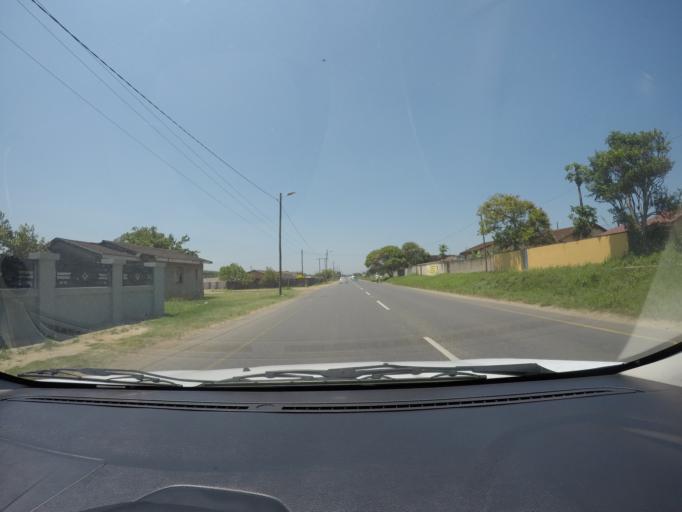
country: ZA
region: KwaZulu-Natal
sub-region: uThungulu District Municipality
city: eSikhawini
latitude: -28.8834
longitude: 31.8875
